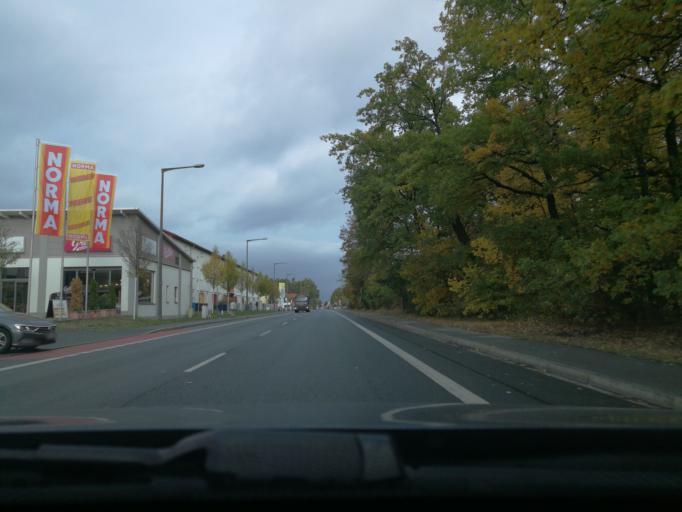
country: DE
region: Bavaria
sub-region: Regierungsbezirk Mittelfranken
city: Furth
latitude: 49.5039
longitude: 10.9802
